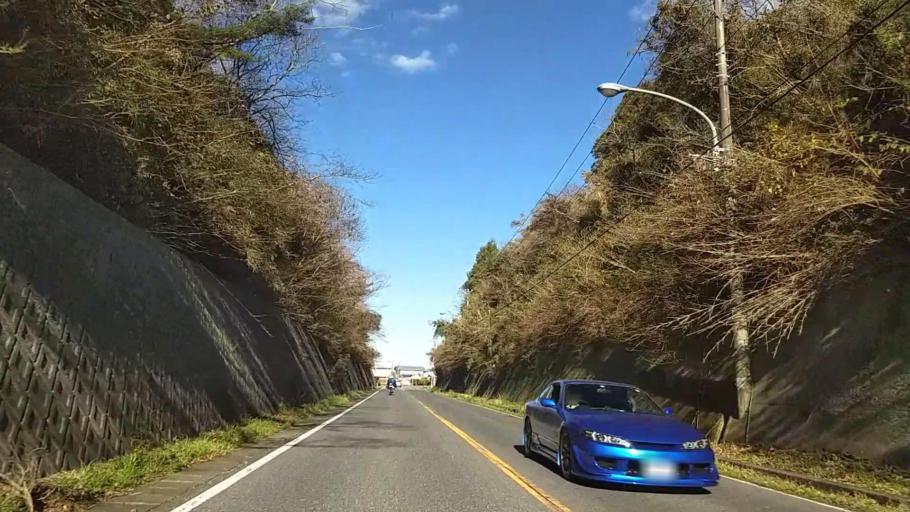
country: JP
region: Chiba
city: Ohara
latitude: 35.2161
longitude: 140.3776
